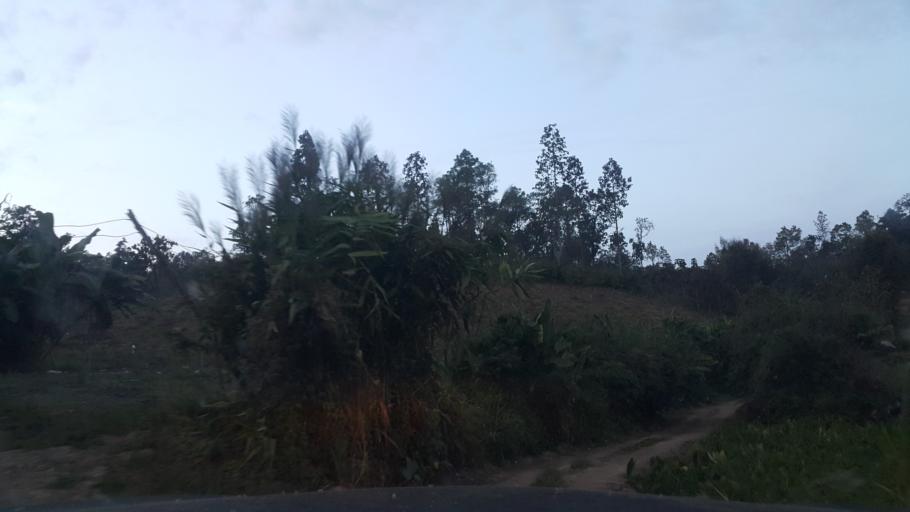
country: TH
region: Chiang Mai
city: Samoeng
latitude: 18.9460
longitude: 98.6721
